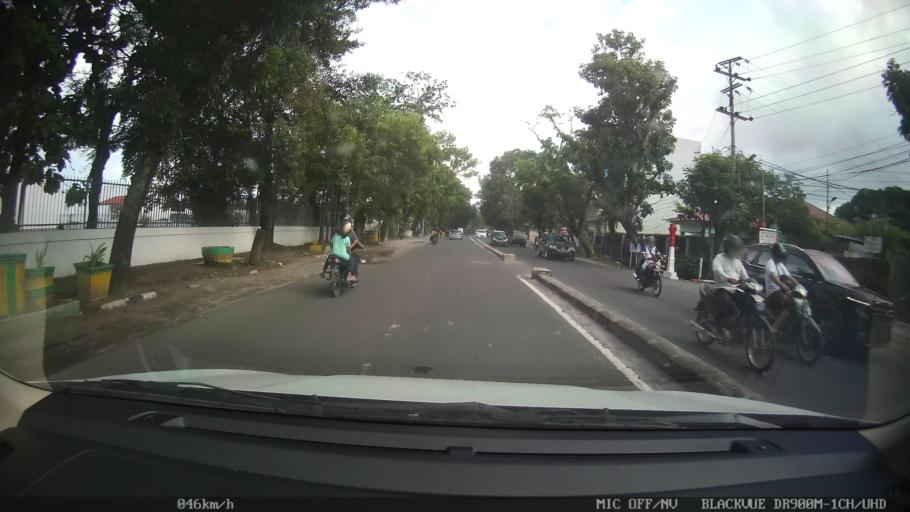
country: ID
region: North Sumatra
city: Medan
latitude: 3.6190
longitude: 98.6715
